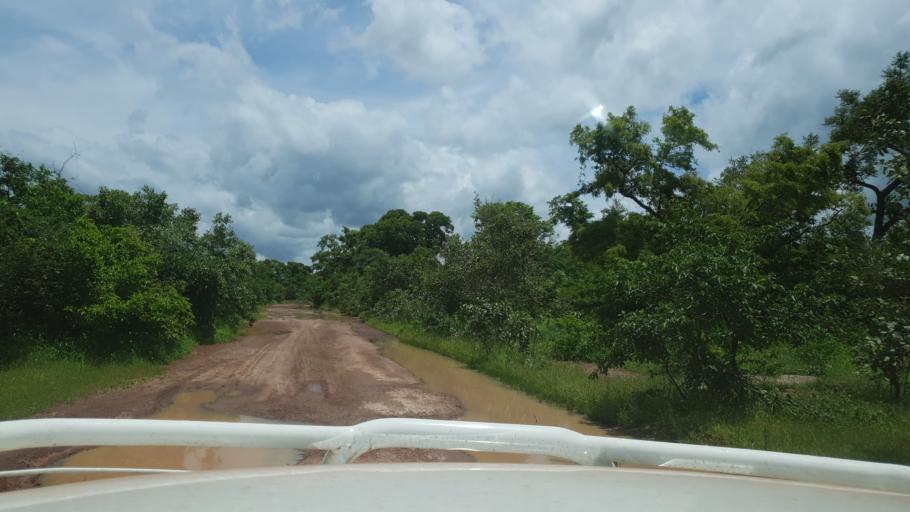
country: ML
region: Koulikoro
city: Banamba
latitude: 13.2008
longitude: -7.3354
